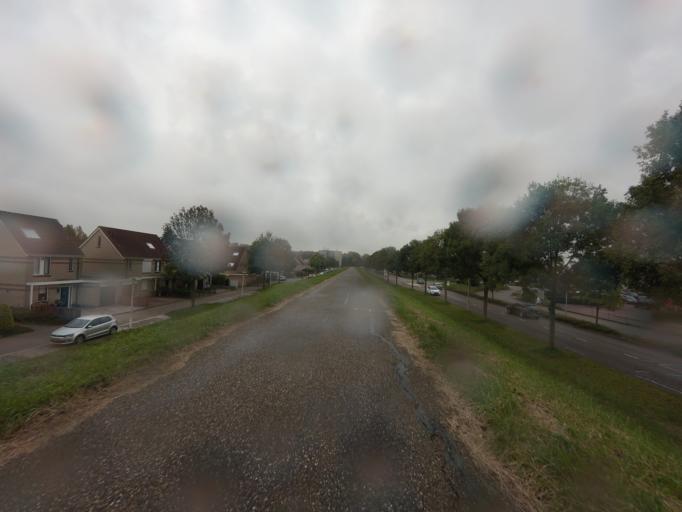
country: NL
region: South Holland
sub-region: Gemeente Gorinchem
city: Gorinchem
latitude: 51.8369
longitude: 4.9846
